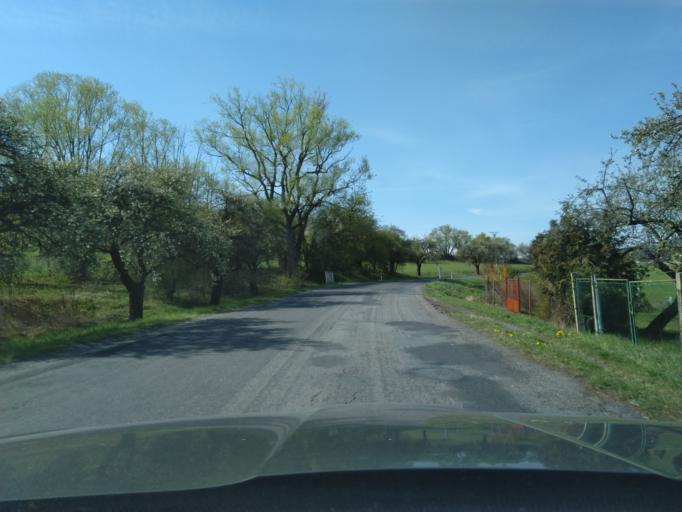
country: CZ
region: Plzensky
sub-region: Okres Klatovy
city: Susice
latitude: 49.2364
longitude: 13.5353
